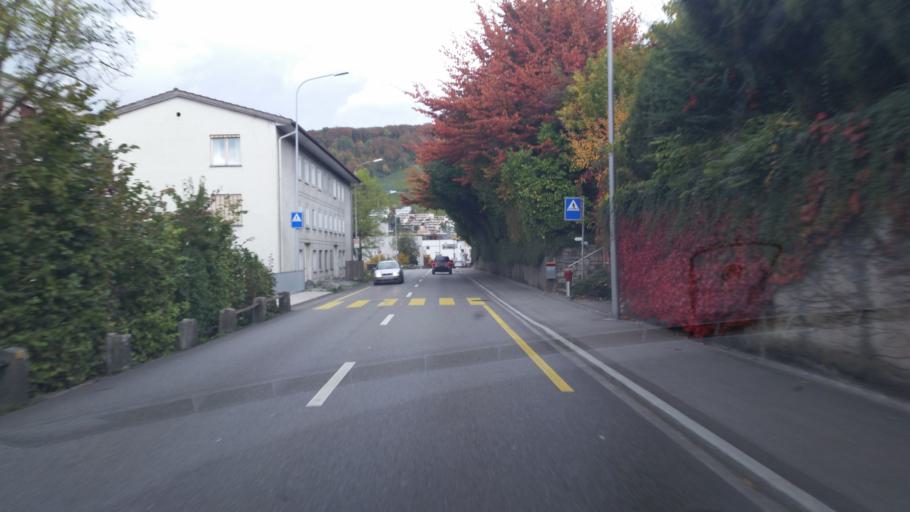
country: CH
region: Aargau
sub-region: Bezirk Baden
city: Baden
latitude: 47.4759
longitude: 8.3114
